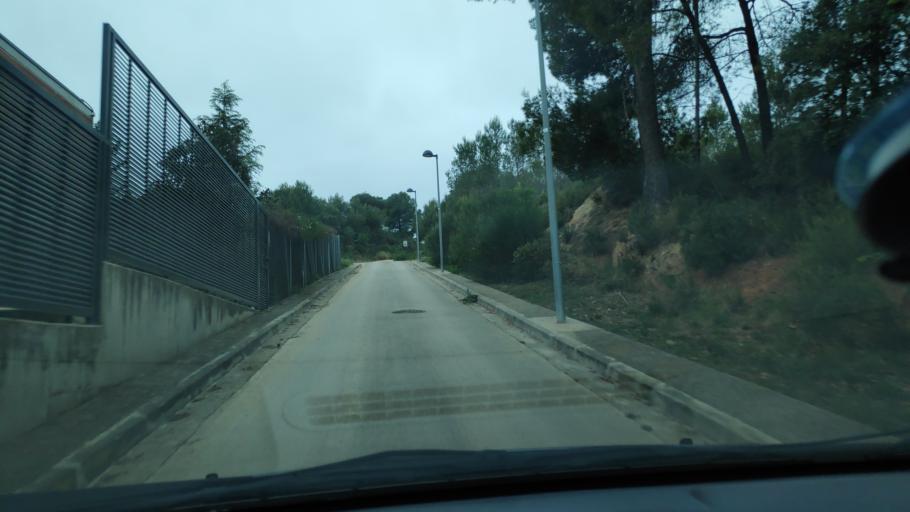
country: ES
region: Catalonia
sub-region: Provincia de Barcelona
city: Sant Quirze del Valles
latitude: 41.5331
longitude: 2.0559
